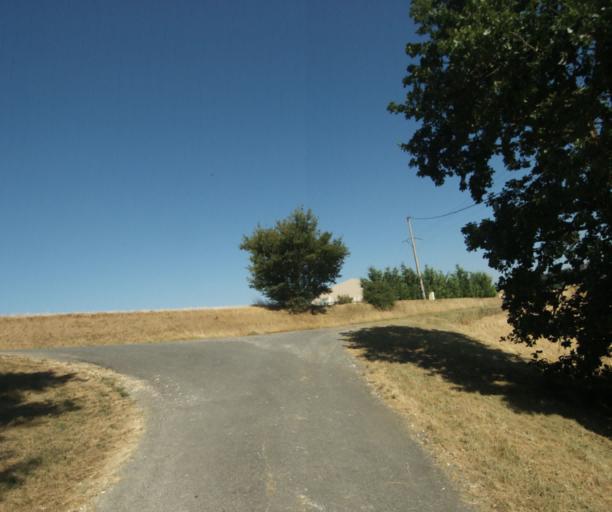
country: FR
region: Midi-Pyrenees
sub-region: Departement de la Haute-Garonne
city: Saint-Felix-Lauragais
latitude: 43.5041
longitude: 1.9345
